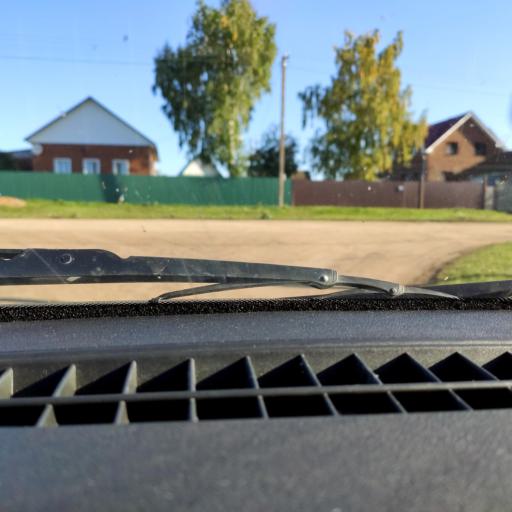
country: RU
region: Bashkortostan
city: Avdon
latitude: 54.5104
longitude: 55.7695
